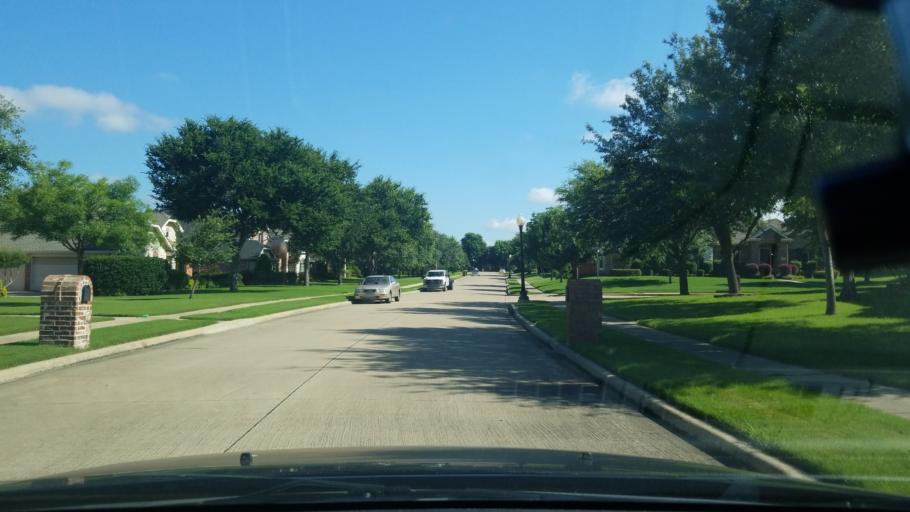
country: US
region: Texas
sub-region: Dallas County
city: Sunnyvale
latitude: 32.8057
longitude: -96.5872
